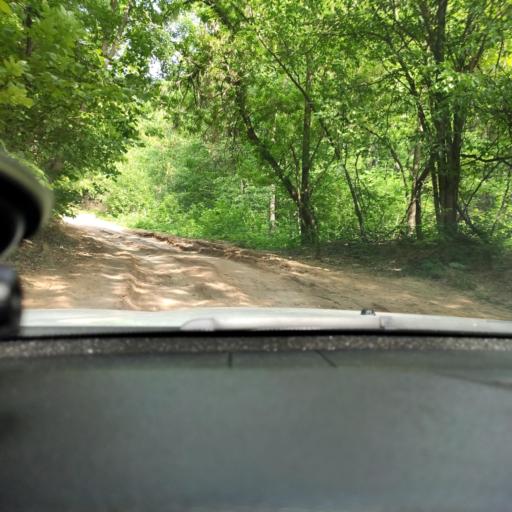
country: RU
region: Samara
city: Novosemeykino
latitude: 53.3357
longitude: 50.2270
